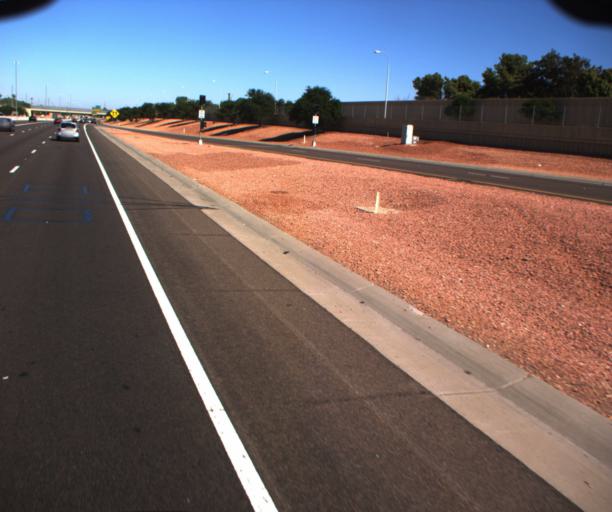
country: US
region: Arizona
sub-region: Maricopa County
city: San Carlos
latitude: 33.3381
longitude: -111.8929
